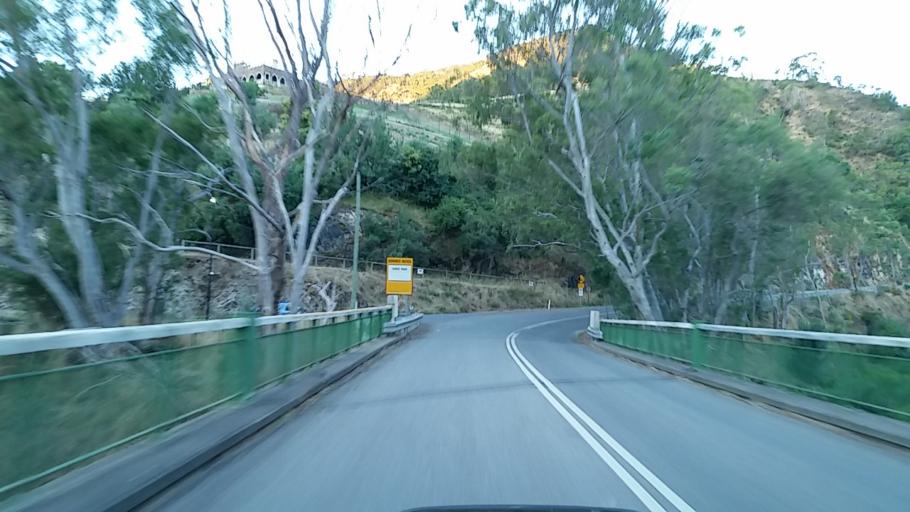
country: AU
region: South Australia
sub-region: Campbelltown
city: Athelstone
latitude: -34.8653
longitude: 138.7583
